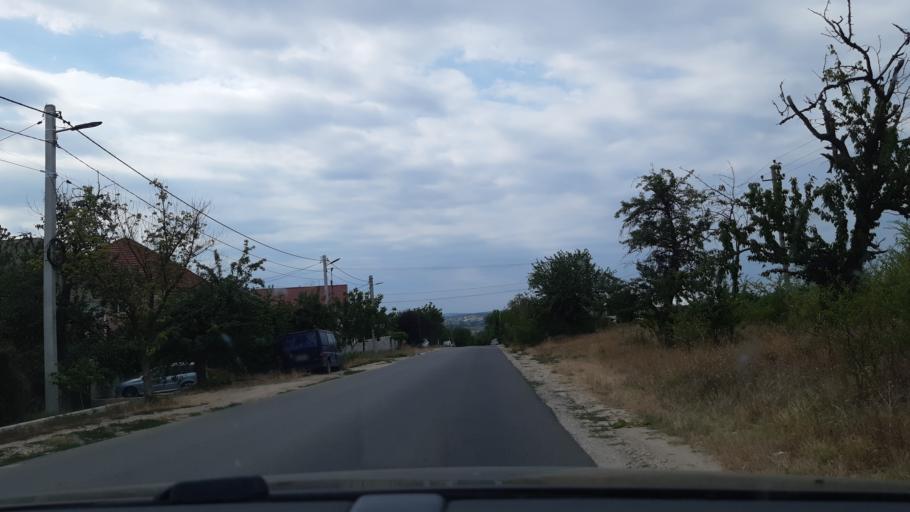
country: MD
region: Chisinau
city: Vatra
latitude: 47.0477
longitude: 28.7408
